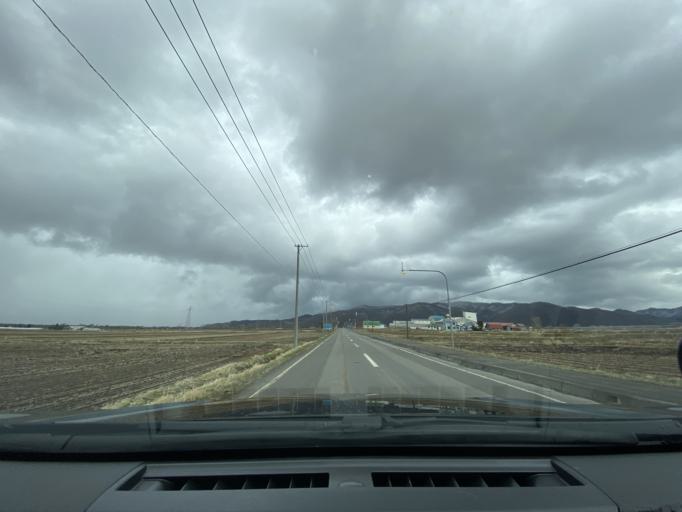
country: JP
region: Hokkaido
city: Nayoro
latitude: 44.1190
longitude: 142.4815
